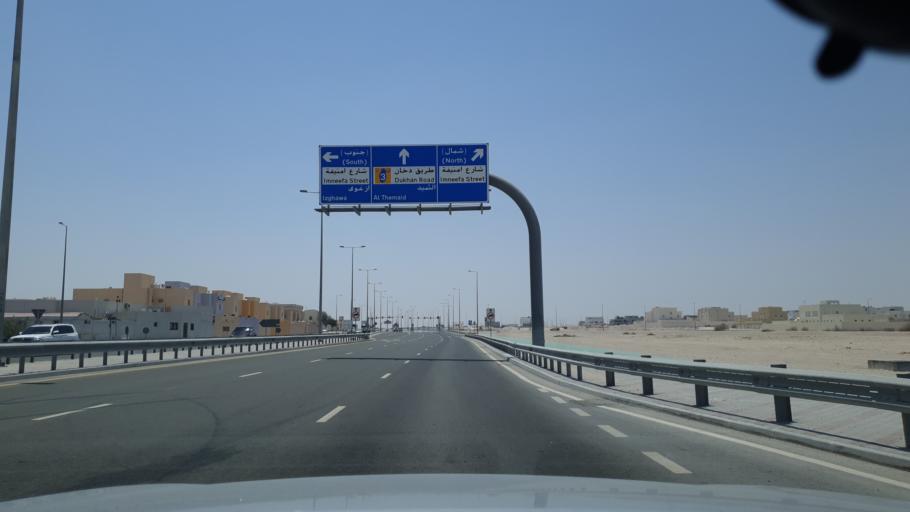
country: QA
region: Baladiyat Umm Salal
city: Umm Salal Muhammad
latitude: 25.3726
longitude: 51.4255
